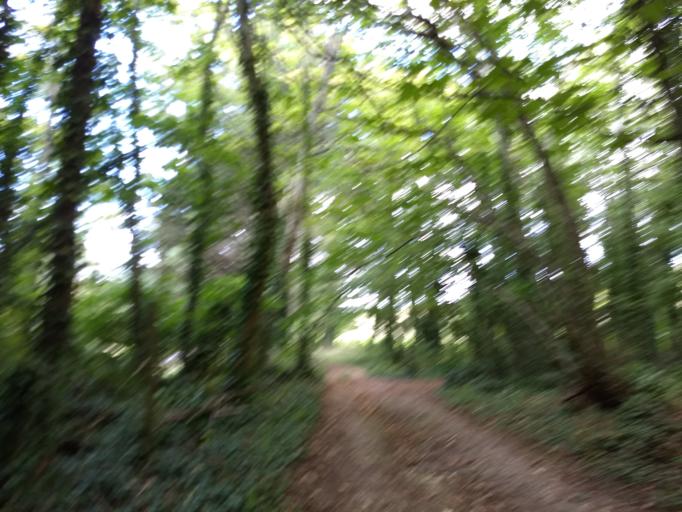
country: GB
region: England
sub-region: Isle of Wight
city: Shalfleet
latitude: 50.6598
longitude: -1.4352
